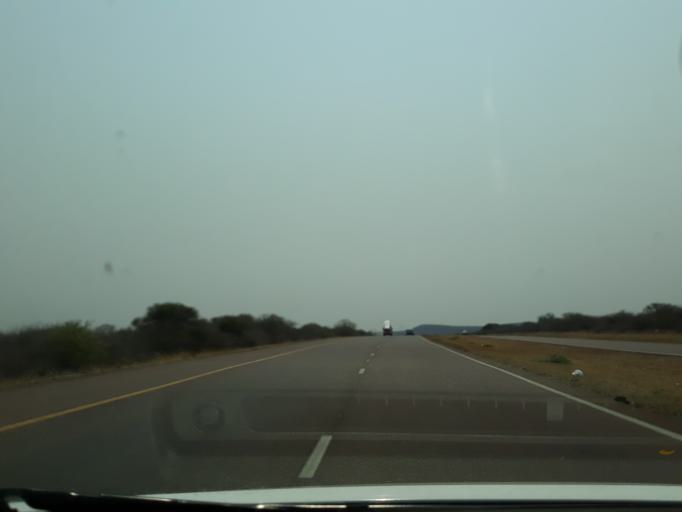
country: BW
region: Kgatleng
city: Bokaa
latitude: -24.4150
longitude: 26.0492
